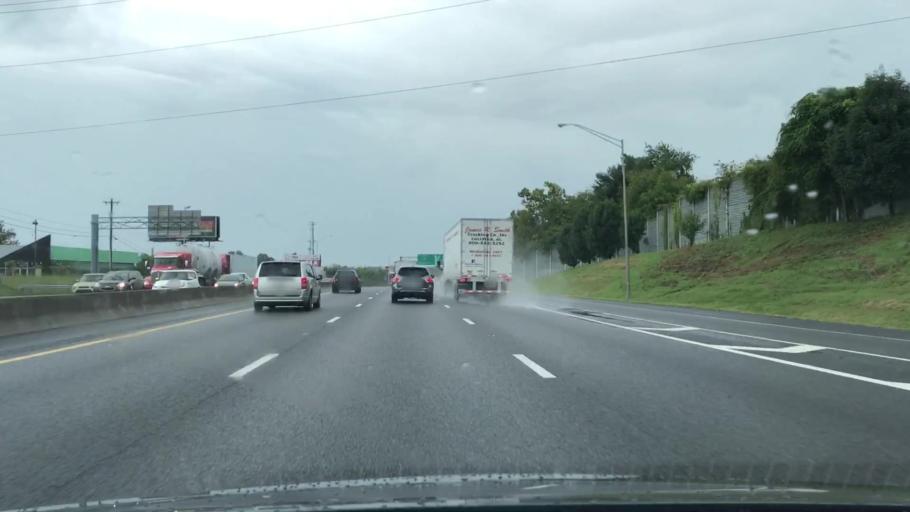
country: US
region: Tennessee
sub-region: Davidson County
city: Nashville
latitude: 36.1323
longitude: -86.7749
